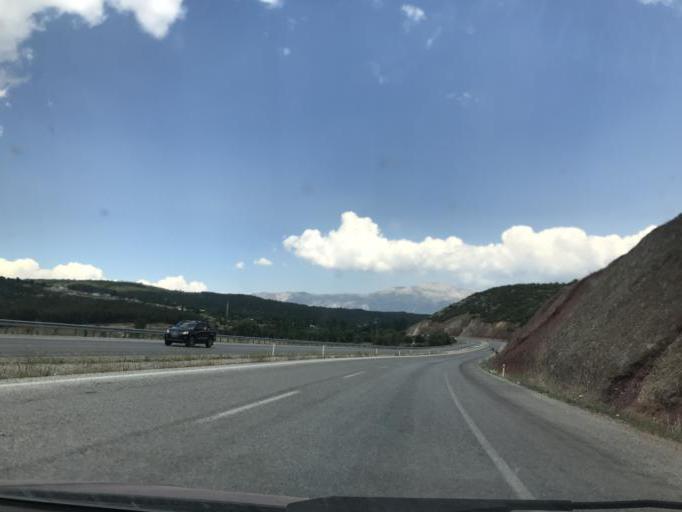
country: TR
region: Denizli
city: Tavas
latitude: 37.6033
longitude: 29.1256
